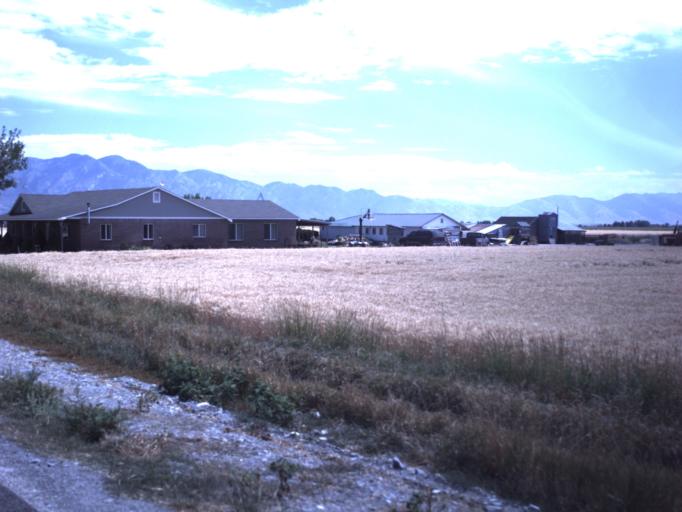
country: US
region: Utah
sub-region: Box Elder County
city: Tremonton
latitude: 41.7098
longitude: -112.2524
